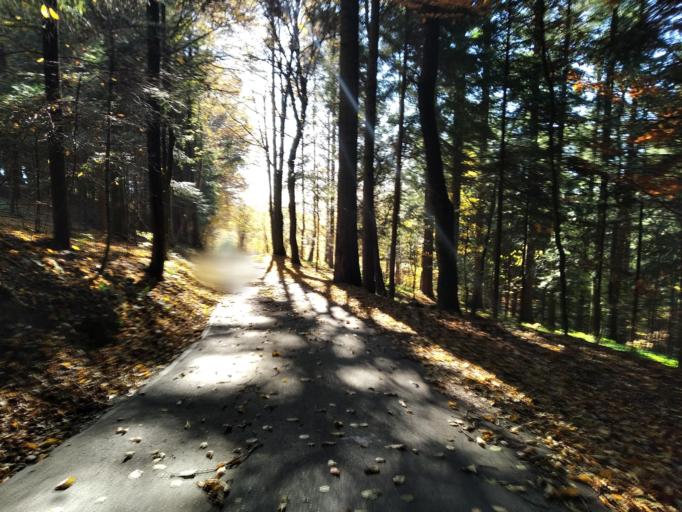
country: PL
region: Subcarpathian Voivodeship
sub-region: Powiat strzyzowski
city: Frysztak
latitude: 49.8541
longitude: 21.6100
